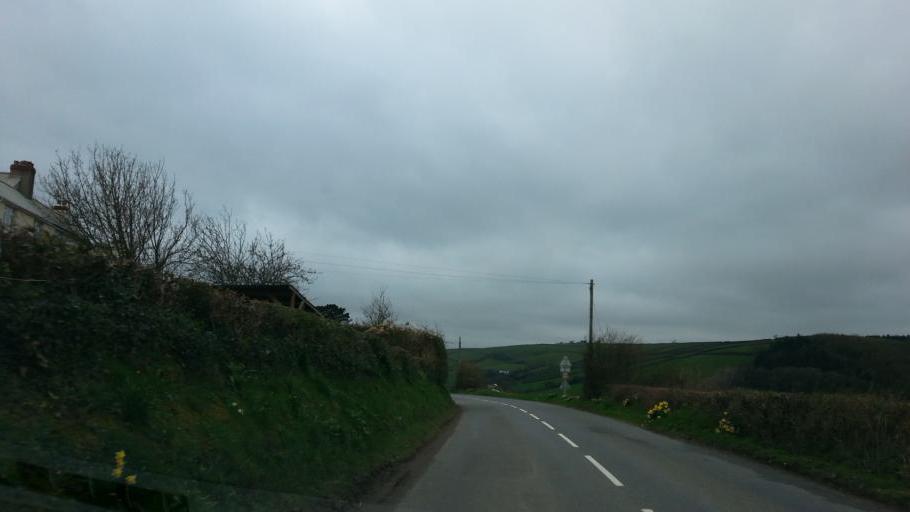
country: GB
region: England
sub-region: Devon
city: Barnstaple
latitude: 51.1007
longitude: -4.0437
